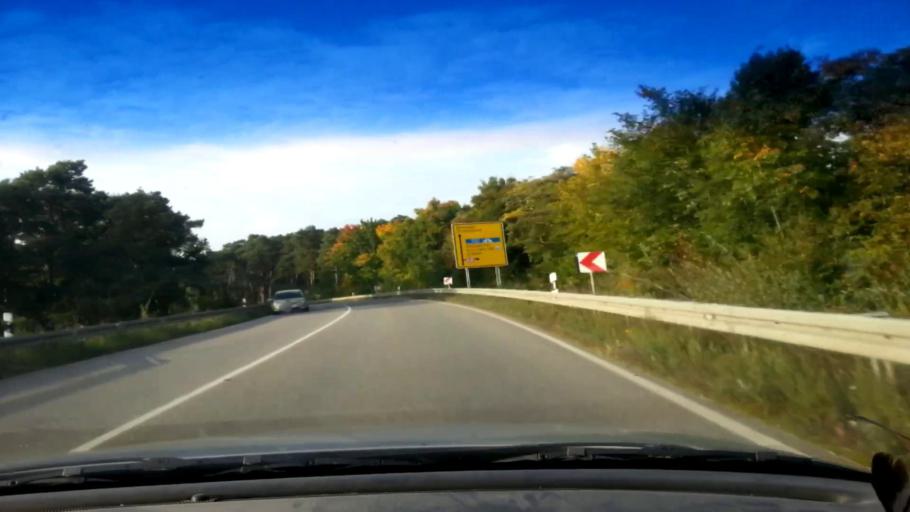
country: DE
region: Bavaria
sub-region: Upper Franconia
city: Hirschaid
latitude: 49.8277
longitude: 10.9825
